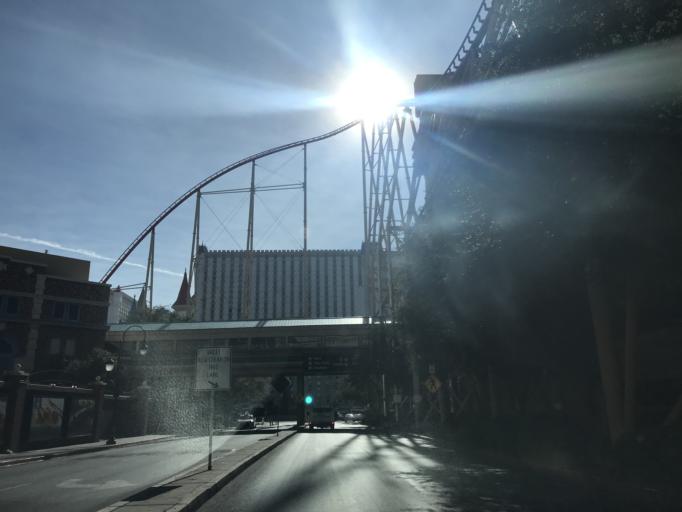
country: US
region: Nevada
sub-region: Clark County
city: Paradise
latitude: 36.1022
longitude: -115.1760
